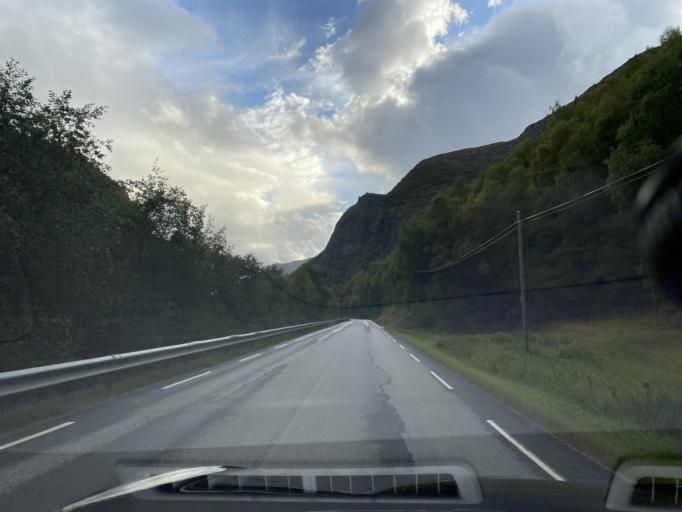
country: NO
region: Oppland
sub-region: Lom
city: Fossbergom
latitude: 61.7855
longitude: 8.4433
